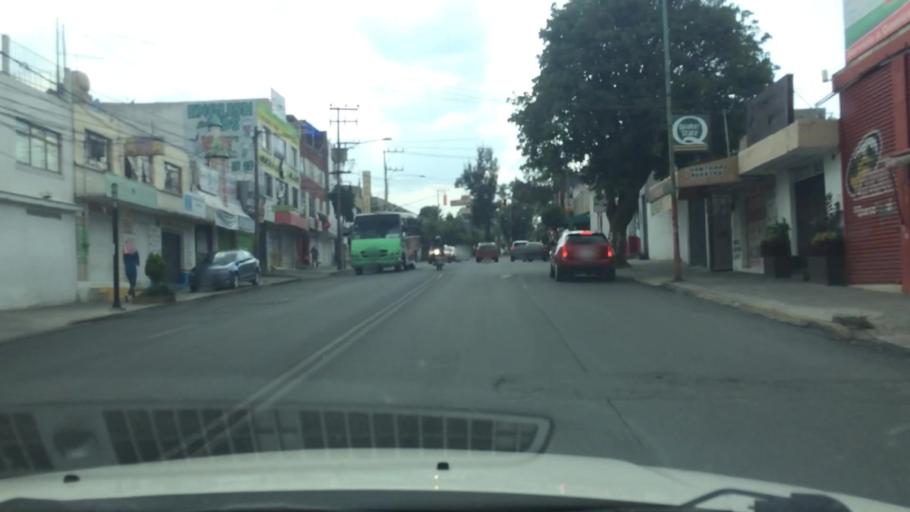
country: MX
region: Mexico City
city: Magdalena Contreras
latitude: 19.3482
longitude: -99.2309
